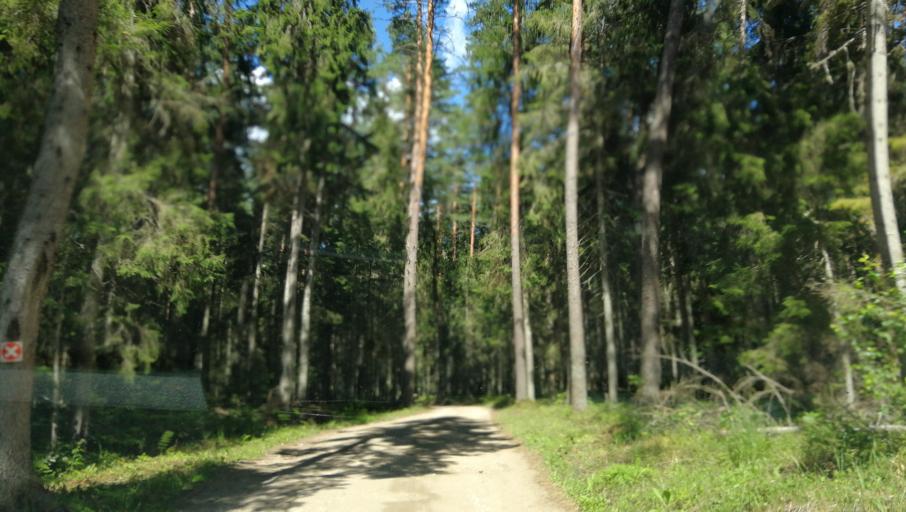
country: LV
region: Cesu Rajons
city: Cesis
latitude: 57.2904
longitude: 25.2126
